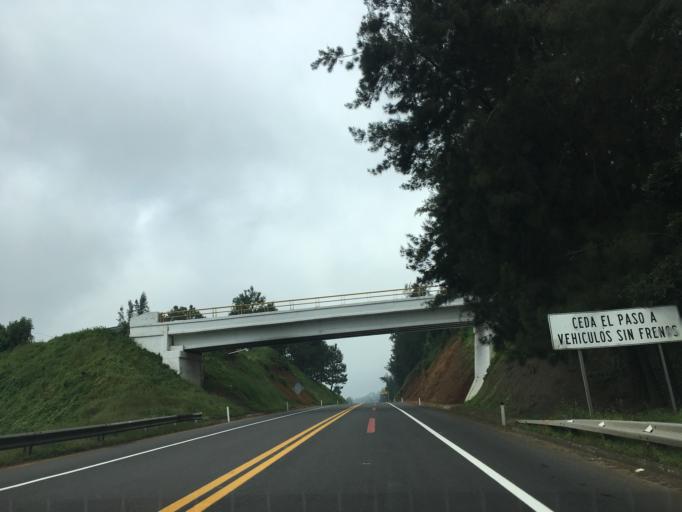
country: MX
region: Michoacan
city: Tingambato
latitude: 19.4349
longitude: -101.8218
